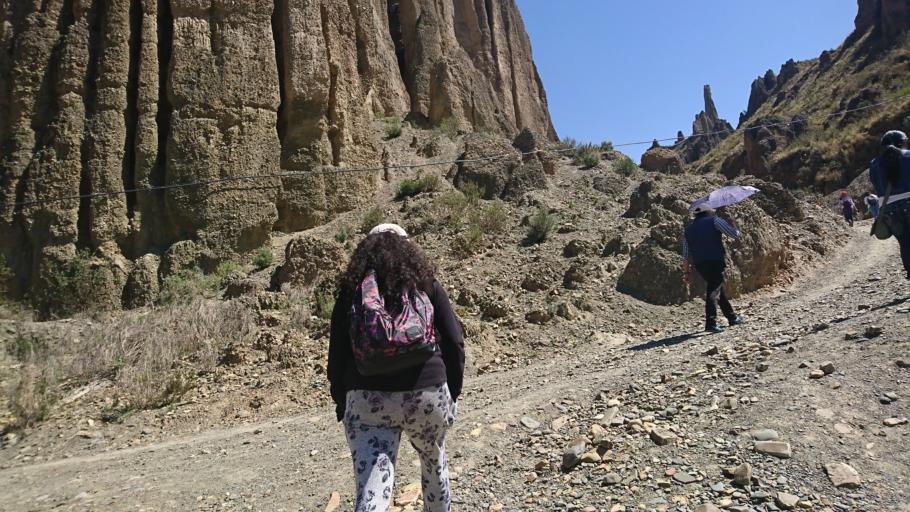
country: BO
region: La Paz
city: La Paz
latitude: -16.5413
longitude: -68.0051
